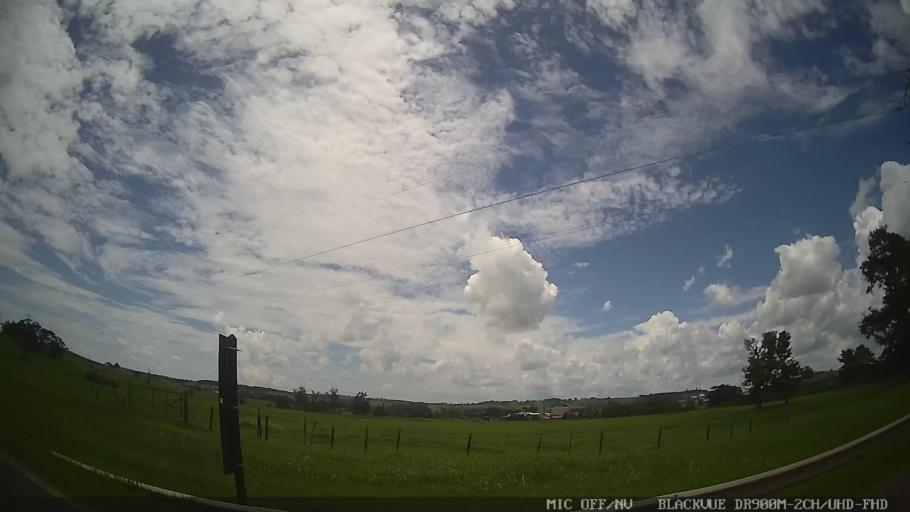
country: BR
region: Sao Paulo
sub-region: Conchas
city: Conchas
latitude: -23.0454
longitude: -47.9471
